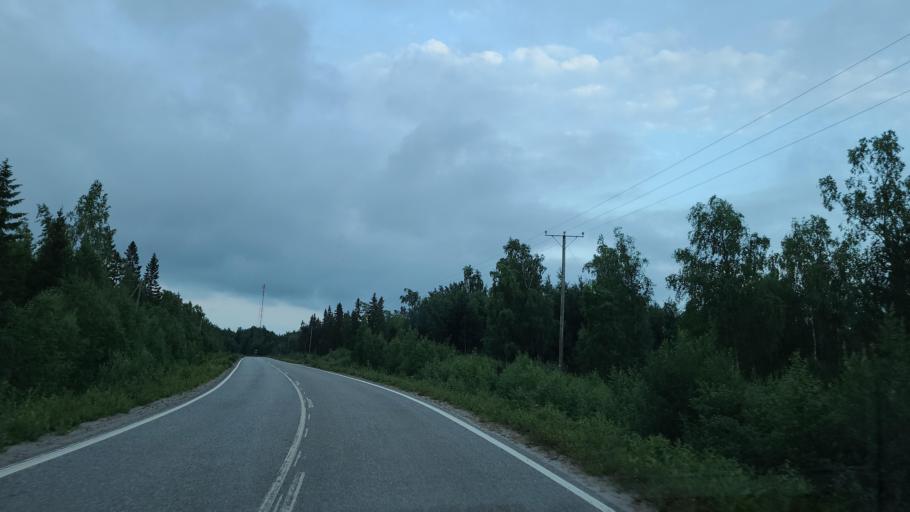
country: FI
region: Ostrobothnia
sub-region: Vaasa
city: Replot
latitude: 63.2914
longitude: 21.1099
